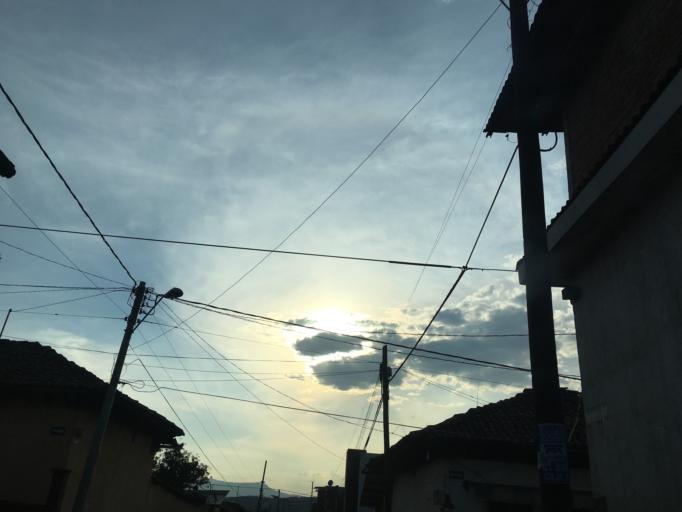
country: MX
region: Michoacan
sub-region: Tingueindin
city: Tingueindin
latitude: 19.7410
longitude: -102.4827
